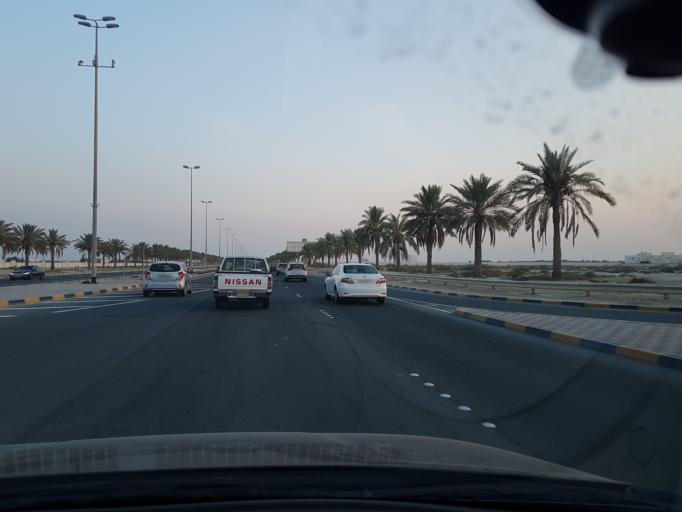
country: BH
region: Central Governorate
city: Dar Kulayb
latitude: 26.0478
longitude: 50.4998
